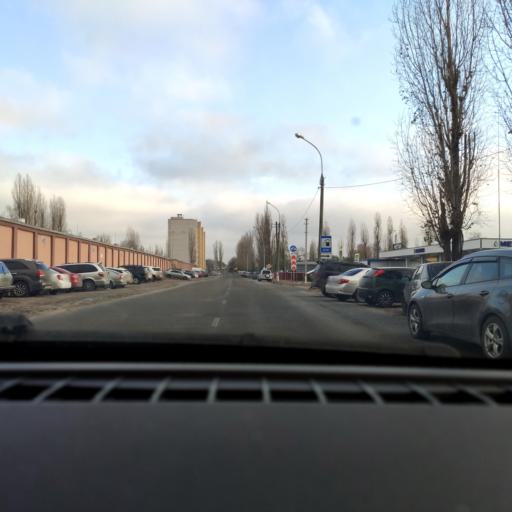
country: RU
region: Voronezj
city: Voronezh
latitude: 51.6783
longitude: 39.2644
